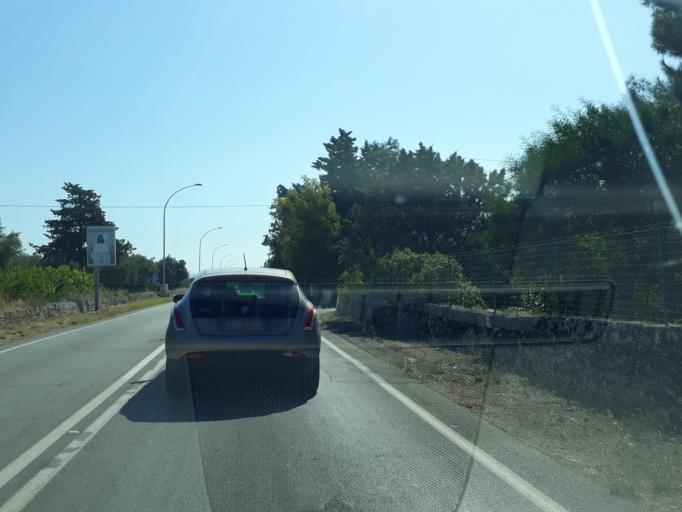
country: IT
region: Apulia
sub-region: Provincia di Bari
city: Monopoli
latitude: 40.9299
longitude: 17.3123
